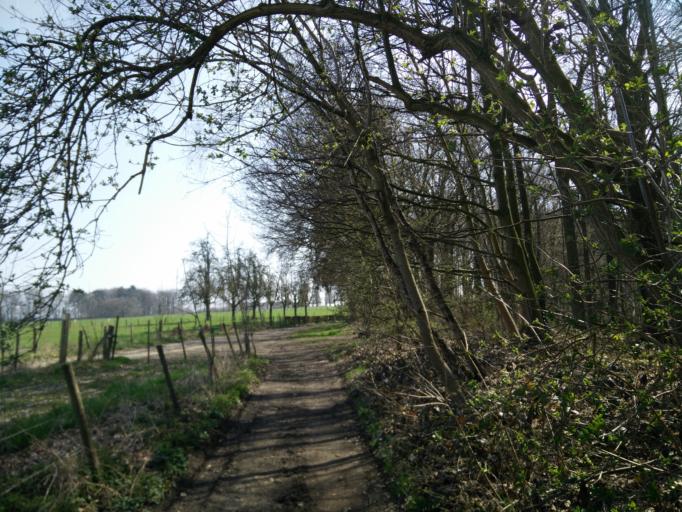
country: BE
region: Flanders
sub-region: Provincie Limburg
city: Sint-Pieters-Voeren
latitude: 50.7435
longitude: 5.7895
